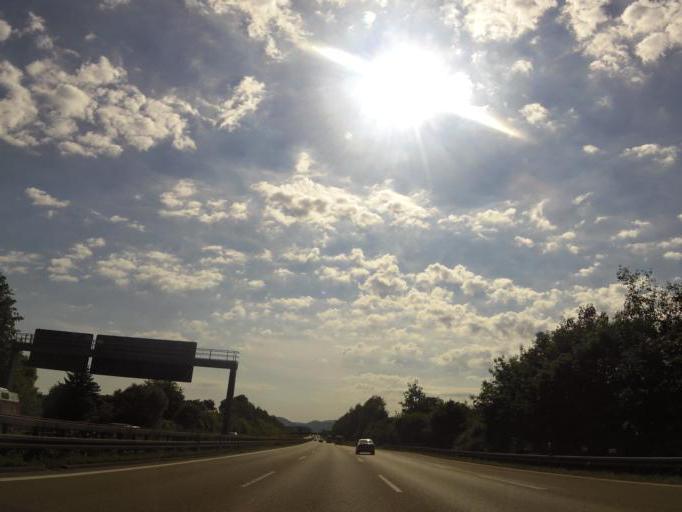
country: DE
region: Baden-Wuerttemberg
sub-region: Regierungsbezirk Stuttgart
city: Dettingen unter Teck
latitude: 48.6305
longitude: 9.4606
